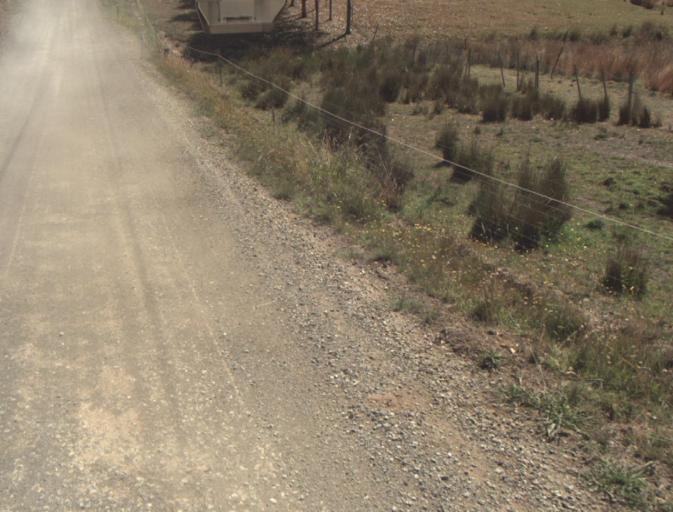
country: AU
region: Tasmania
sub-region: Launceston
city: Mayfield
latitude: -41.2283
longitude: 147.2361
